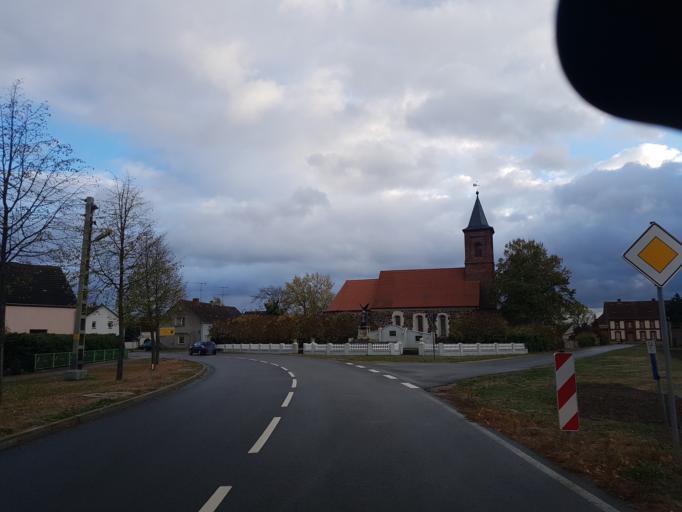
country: DE
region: Saxony-Anhalt
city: Seyda
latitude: 51.8919
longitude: 12.8924
